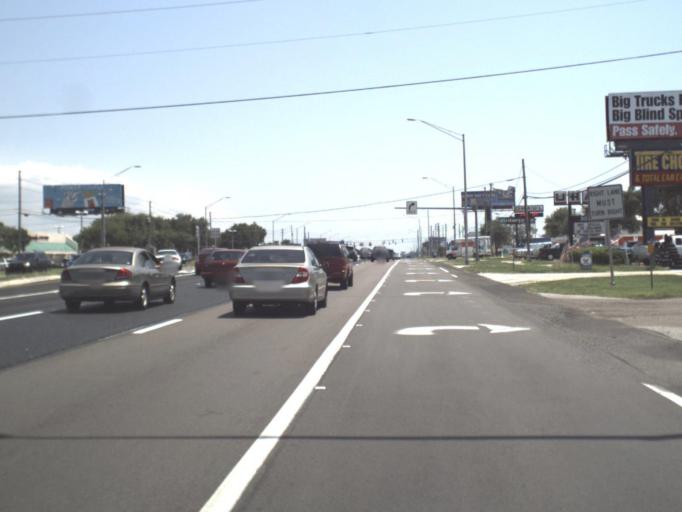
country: US
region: Florida
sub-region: Pinellas County
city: Saint George
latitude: 28.0528
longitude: -82.7389
